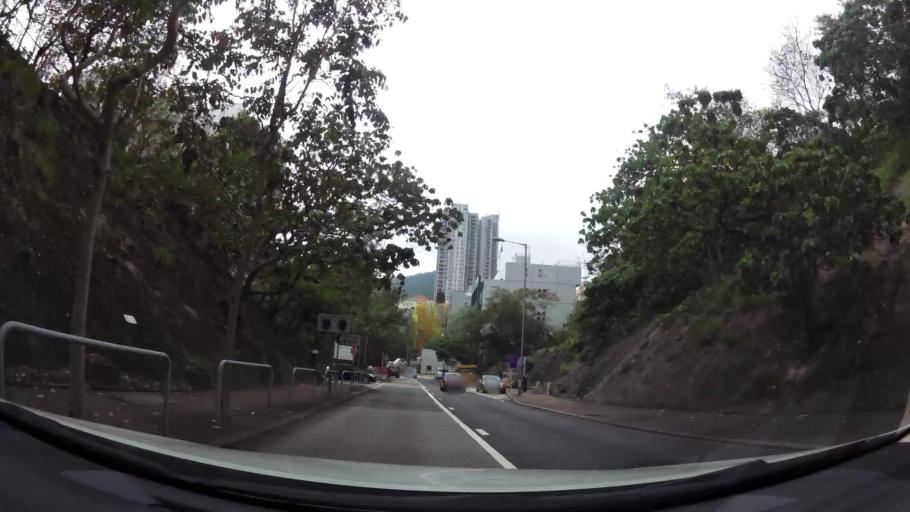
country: HK
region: Central and Western
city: Central
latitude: 22.2679
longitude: 114.1272
